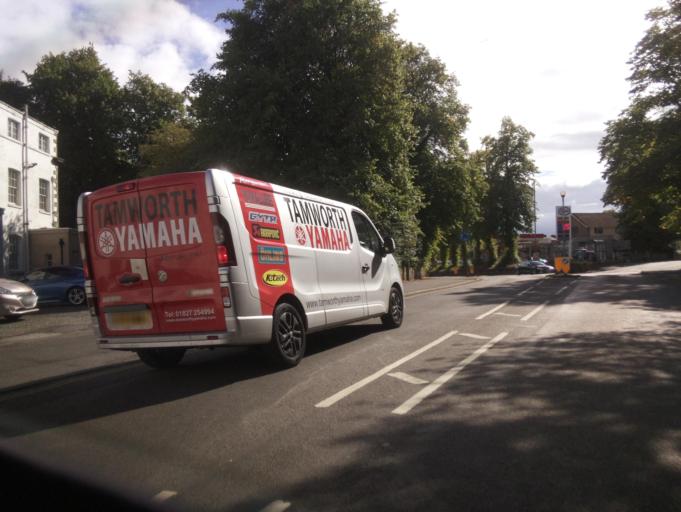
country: GB
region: England
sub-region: Leicestershire
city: Ashby de la Zouch
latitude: 52.7453
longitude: -1.4742
